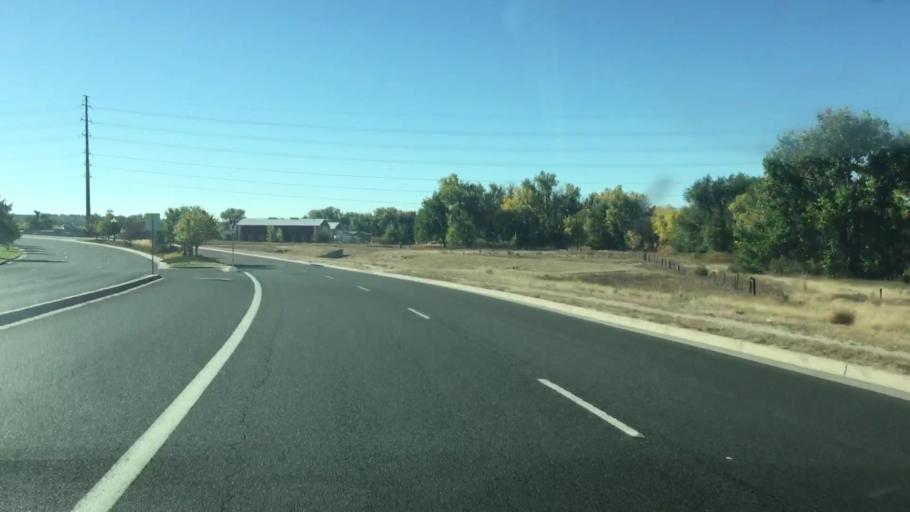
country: US
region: Colorado
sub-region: Douglas County
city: Parker
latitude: 39.5130
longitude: -104.7746
